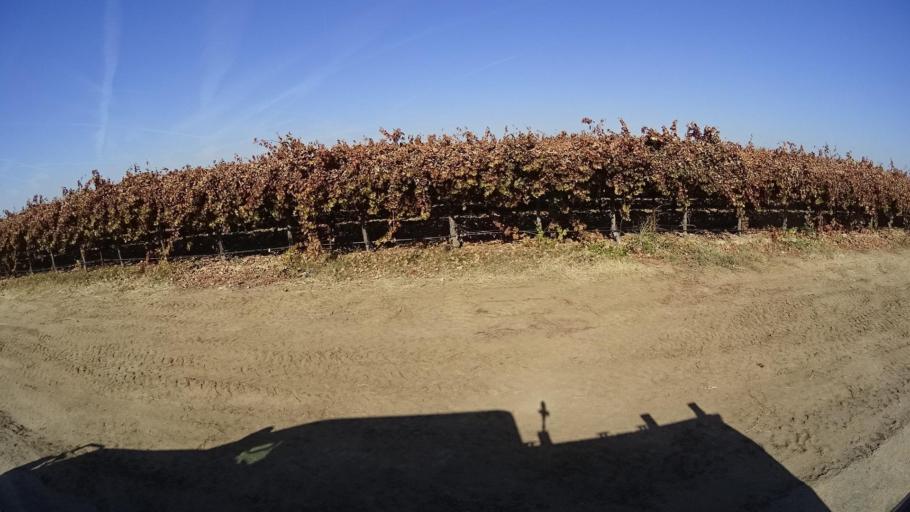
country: US
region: California
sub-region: Kern County
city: McFarland
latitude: 35.6456
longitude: -119.1940
